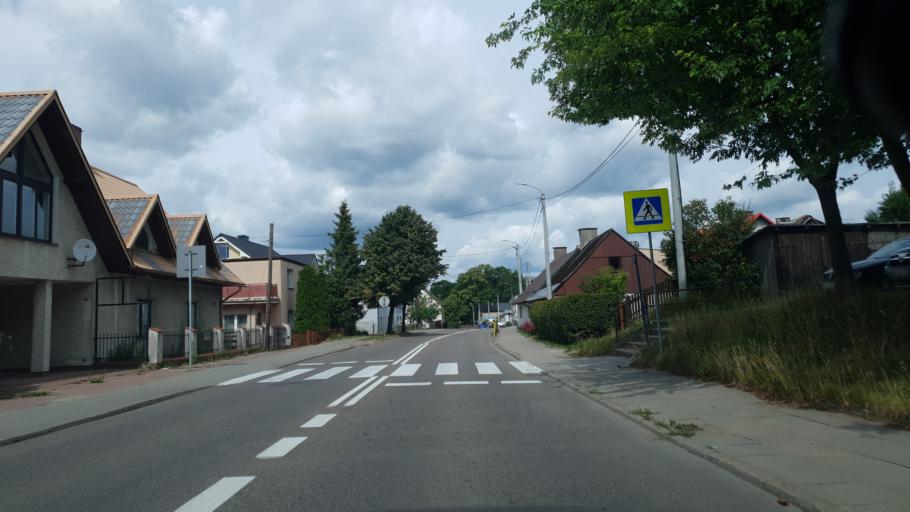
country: PL
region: Pomeranian Voivodeship
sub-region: Powiat kartuski
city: Kartuzy
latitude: 54.3280
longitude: 18.1946
